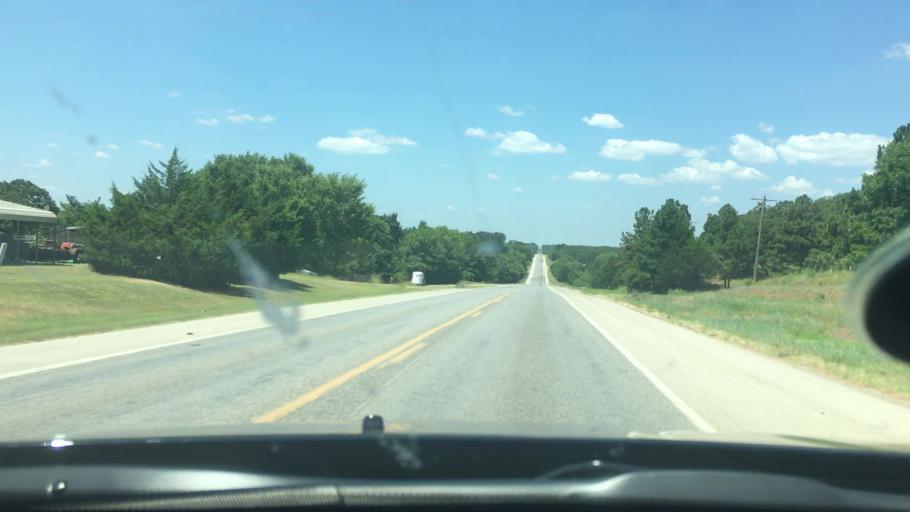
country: US
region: Oklahoma
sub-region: Carter County
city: Dickson
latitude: 34.1873
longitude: -96.9136
